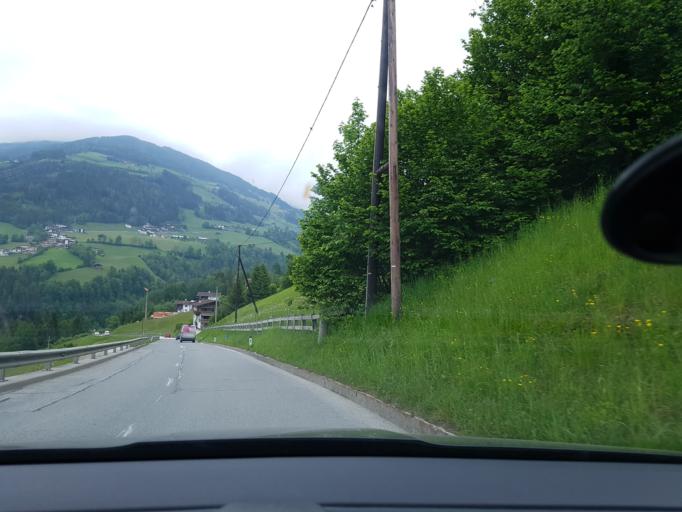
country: AT
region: Tyrol
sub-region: Politischer Bezirk Schwaz
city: Hainzenberg
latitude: 47.2225
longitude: 11.8892
